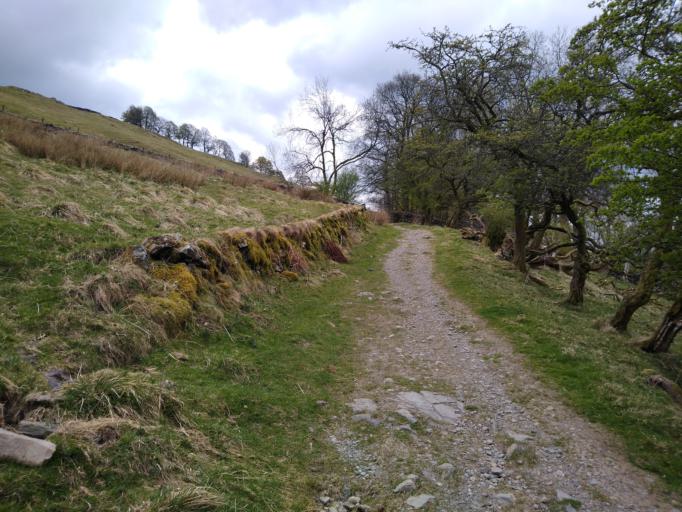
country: GB
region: England
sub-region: Cumbria
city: Windermere
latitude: 54.4172
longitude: -2.8999
